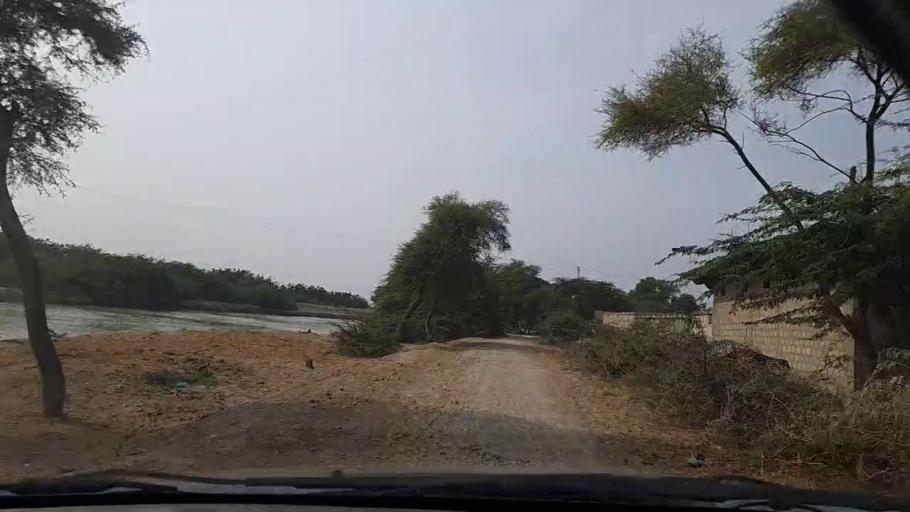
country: PK
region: Sindh
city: Thatta
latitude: 24.5684
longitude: 67.8630
